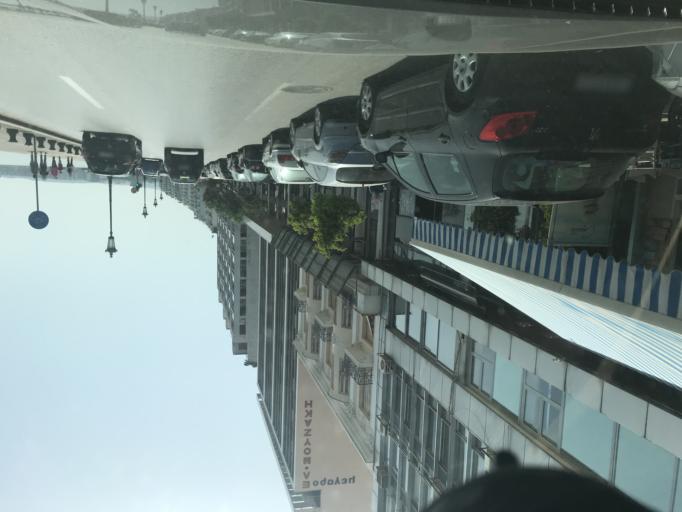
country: GR
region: Central Macedonia
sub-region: Nomos Thessalonikis
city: Thessaloniki
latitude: 40.6332
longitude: 22.9384
